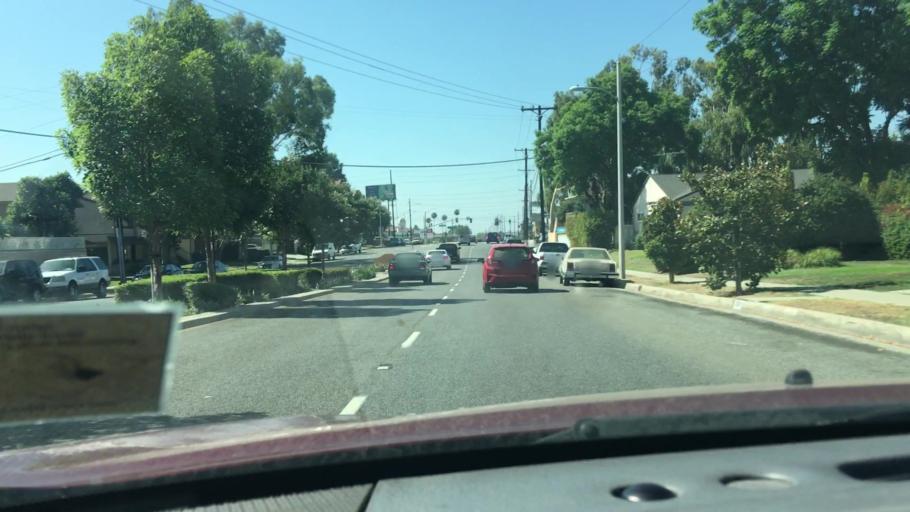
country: US
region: California
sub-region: Los Angeles County
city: La Mirada
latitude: 33.9291
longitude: -118.0119
